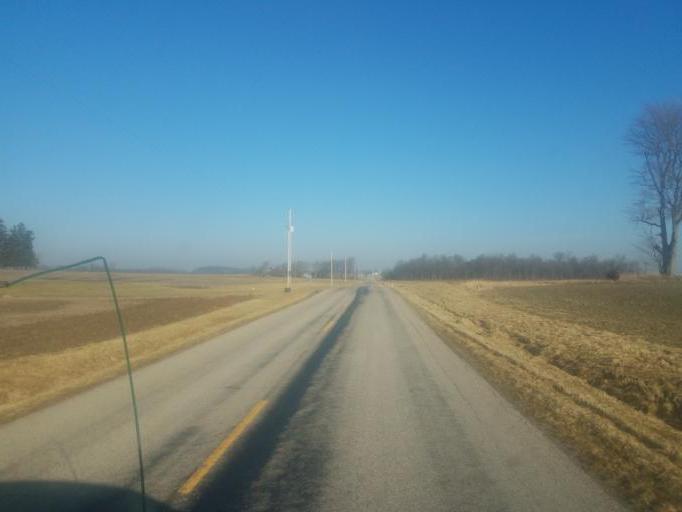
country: US
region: Ohio
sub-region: Crawford County
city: Bucyrus
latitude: 40.8810
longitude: -82.9400
